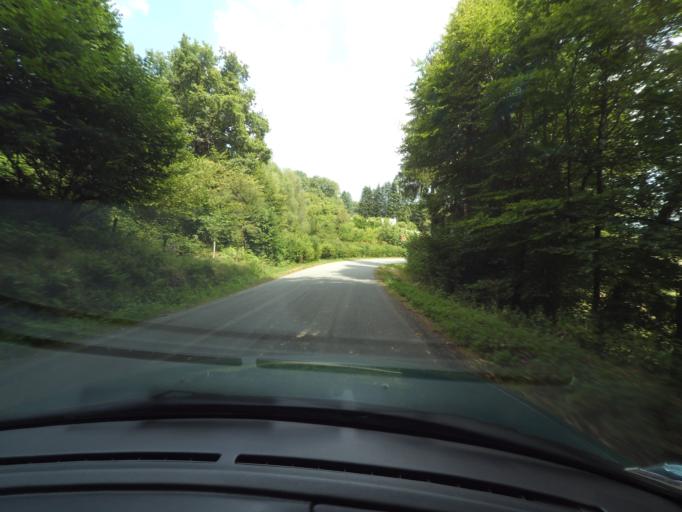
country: FR
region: Limousin
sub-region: Departement de la Haute-Vienne
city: Peyrat-le-Chateau
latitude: 45.7310
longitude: 1.8818
